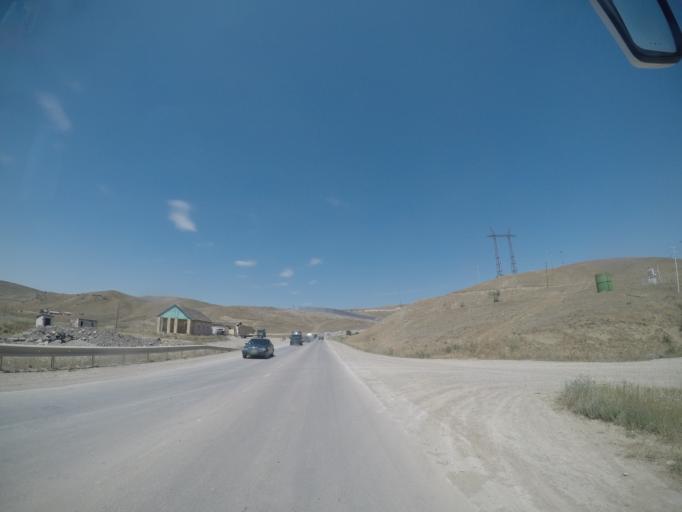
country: AZ
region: Samaxi
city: Shamakhi
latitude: 40.5565
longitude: 48.7587
